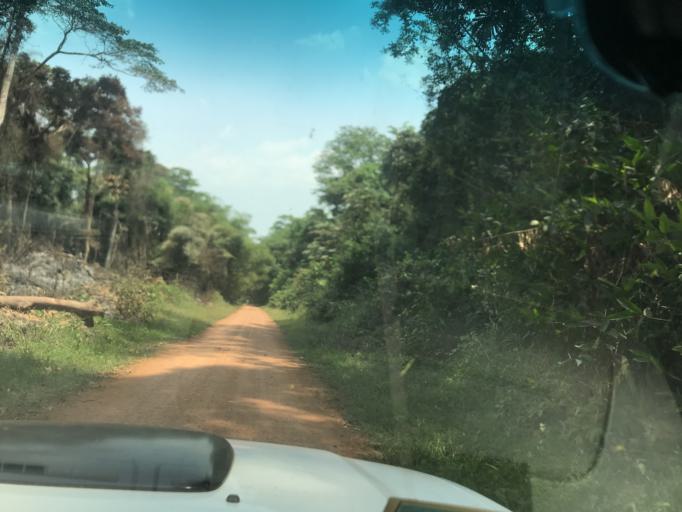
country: CD
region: Eastern Province
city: Aketi
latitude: 2.4907
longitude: 23.2932
